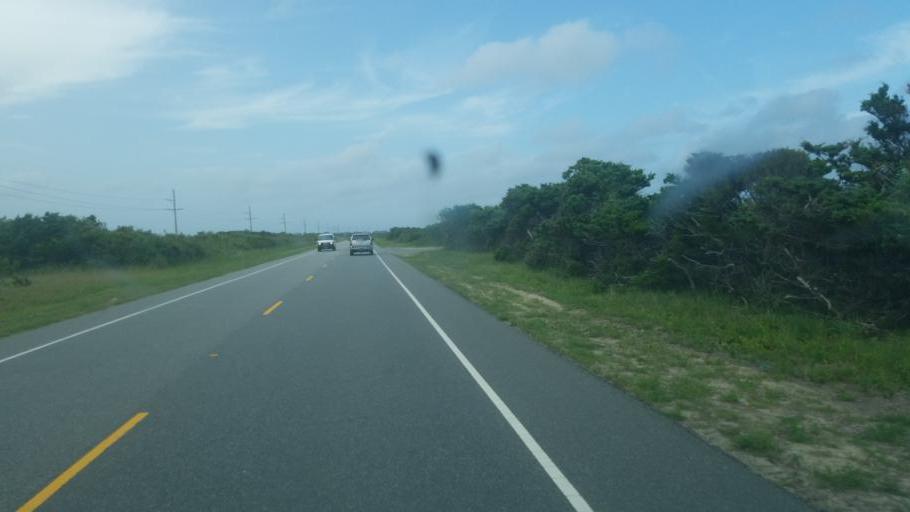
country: US
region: North Carolina
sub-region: Dare County
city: Buxton
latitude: 35.3078
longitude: -75.5119
